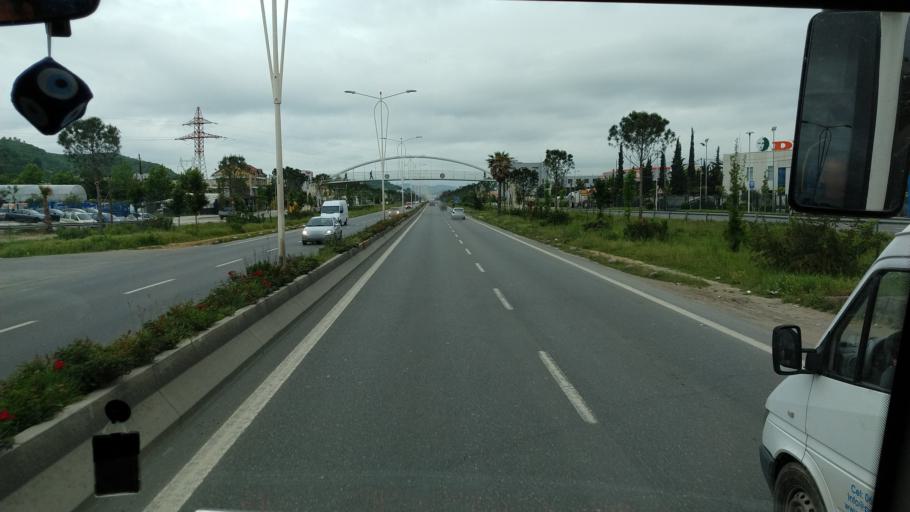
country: AL
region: Tirane
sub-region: Rrethi i Tiranes
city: Kamez
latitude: 41.3542
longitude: 19.7438
